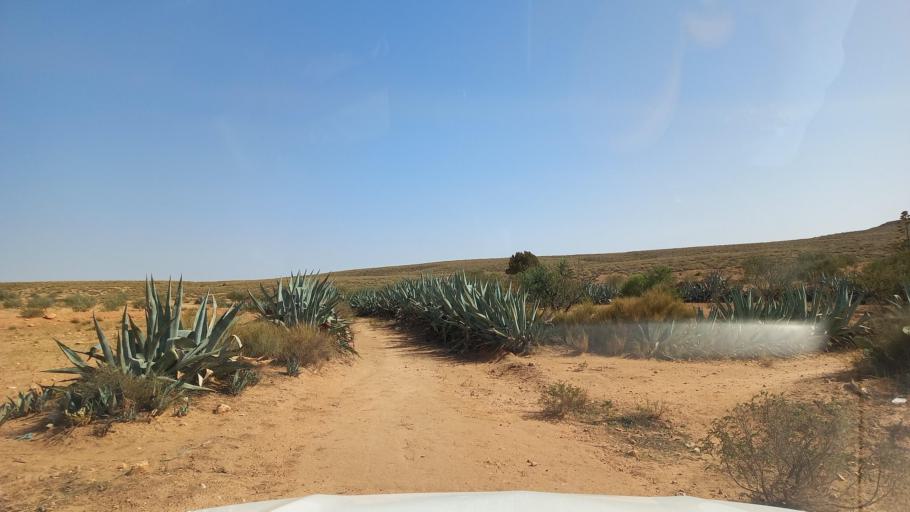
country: TN
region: Al Qasrayn
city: Kasserine
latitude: 35.2082
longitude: 8.9854
